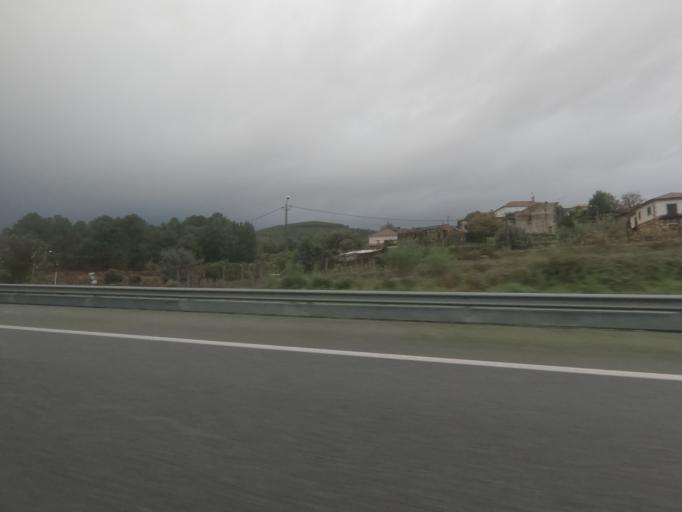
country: PT
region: Viana do Castelo
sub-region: Ponte de Lima
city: Ponte de Lima
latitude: 41.8031
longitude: -8.5849
